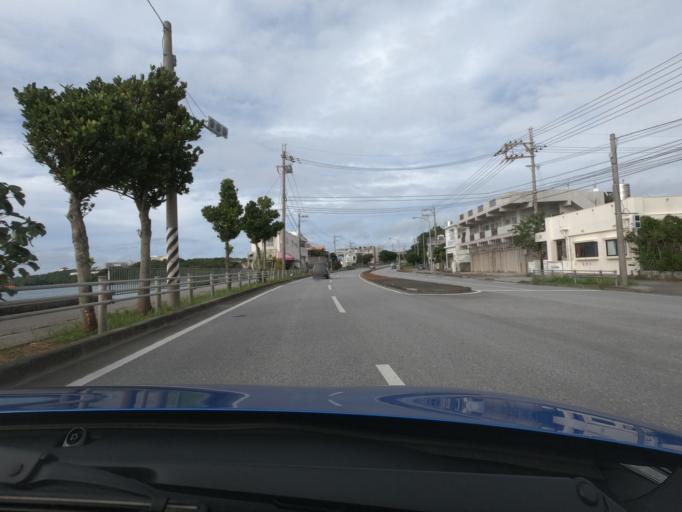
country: JP
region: Okinawa
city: Nago
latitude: 26.6709
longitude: 127.8895
